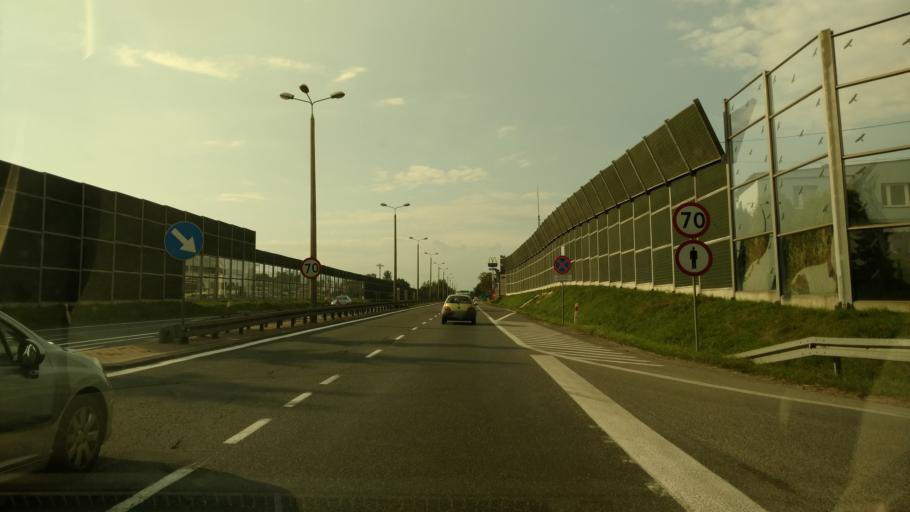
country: PL
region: Silesian Voivodeship
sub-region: Powiat pszczynski
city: Pszczyna
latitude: 49.9842
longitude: 18.9566
